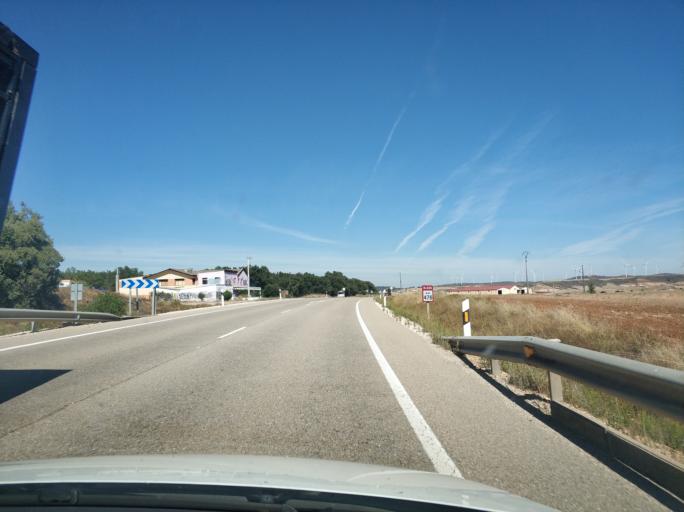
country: ES
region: Castille and Leon
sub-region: Provincia de Burgos
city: Revillarruz
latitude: 42.2154
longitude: -3.6529
